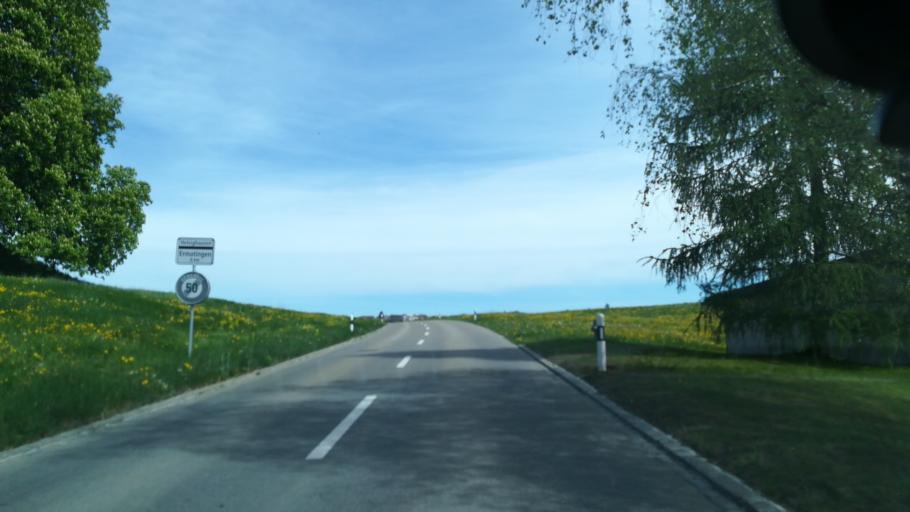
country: CH
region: Thurgau
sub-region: Weinfelden District
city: Maerstetten-Dorf
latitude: 47.6254
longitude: 9.0675
